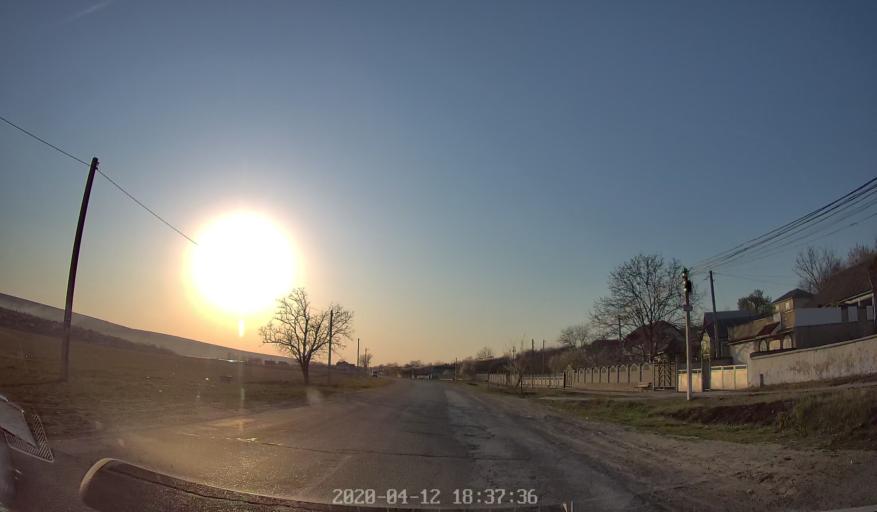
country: MD
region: Chisinau
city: Vadul lui Voda
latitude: 47.1218
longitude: 29.0130
